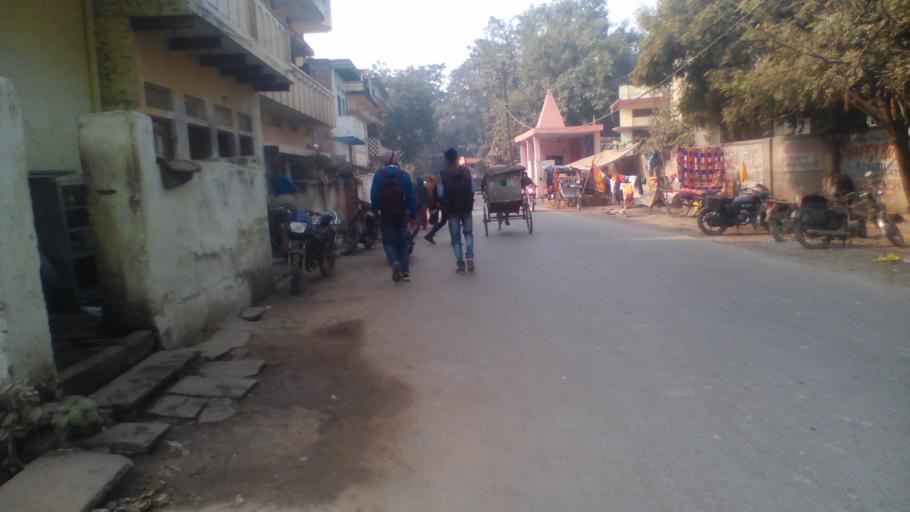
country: IN
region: Uttar Pradesh
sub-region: Varanasi
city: Varanasi
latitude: 25.3529
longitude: 82.9734
